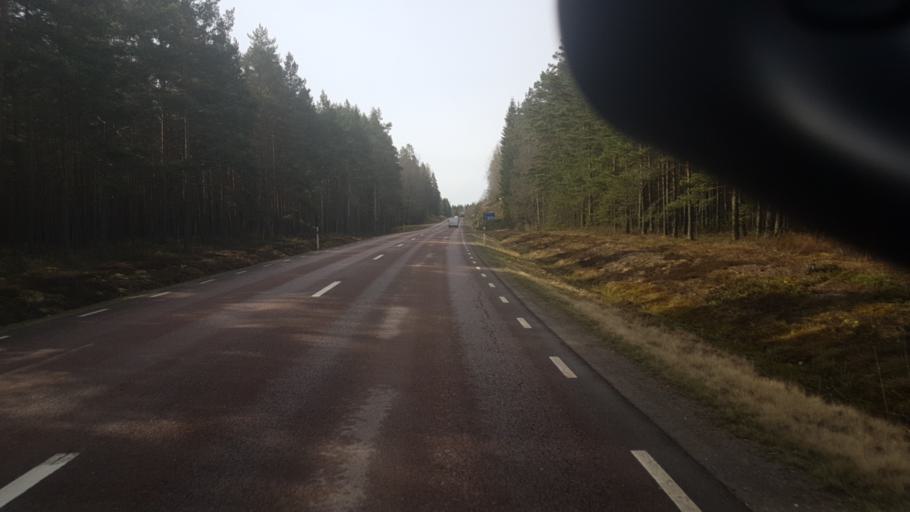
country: SE
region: Vaermland
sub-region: Arvika Kommun
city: Arvika
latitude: 59.6304
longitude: 12.6184
